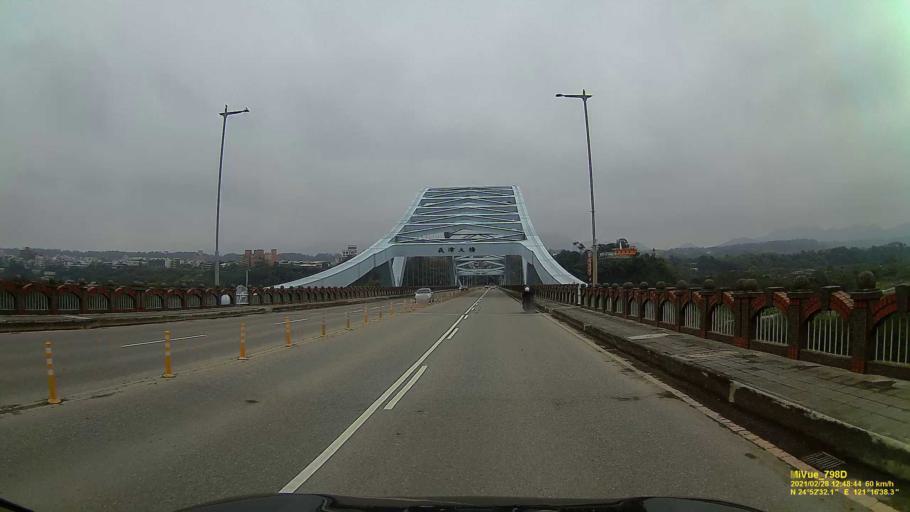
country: TW
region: Taiwan
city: Daxi
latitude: 24.8755
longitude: 121.2775
